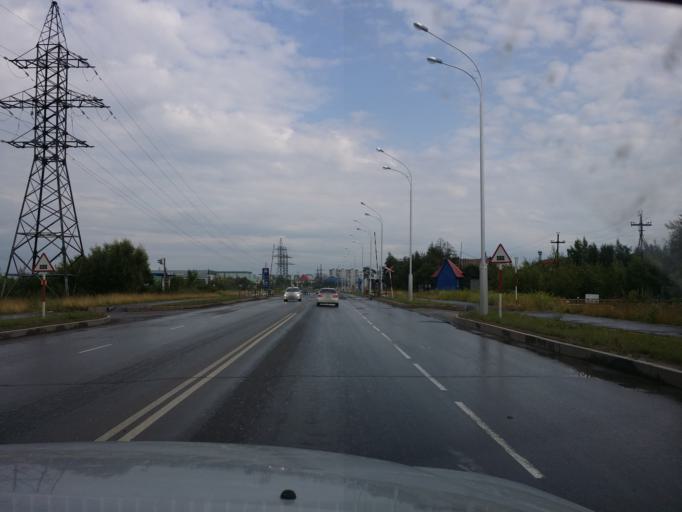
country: RU
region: Khanty-Mansiyskiy Avtonomnyy Okrug
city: Nizhnevartovsk
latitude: 60.9626
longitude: 76.5538
